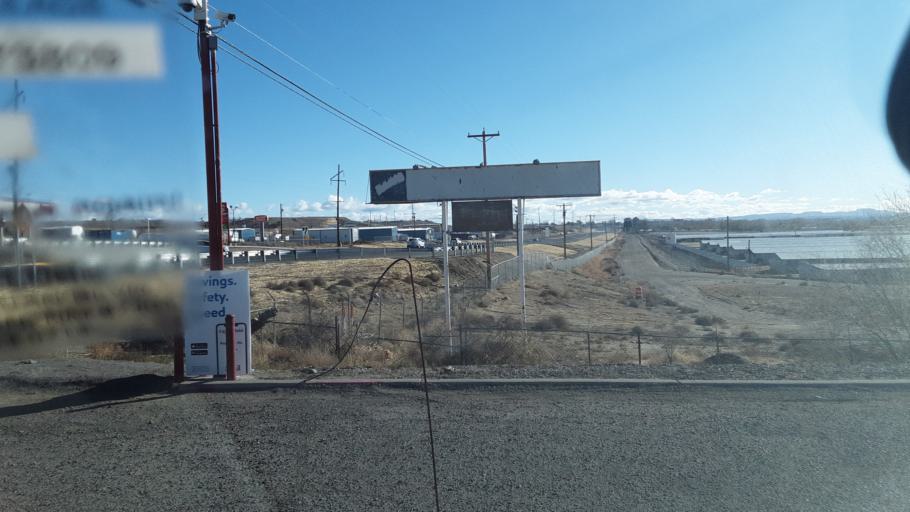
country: US
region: New Mexico
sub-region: San Juan County
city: Lee Acres
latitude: 36.7037
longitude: -108.1055
